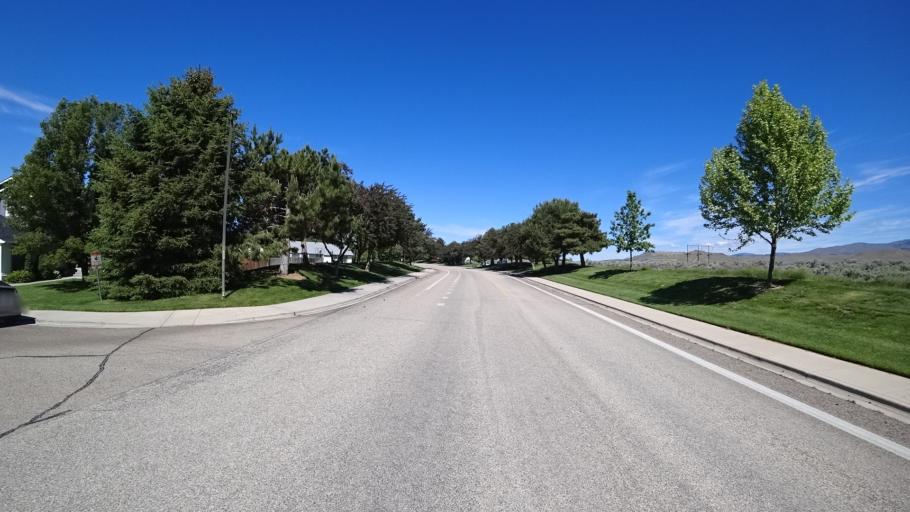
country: US
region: Idaho
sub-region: Ada County
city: Boise
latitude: 43.5500
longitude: -116.1225
